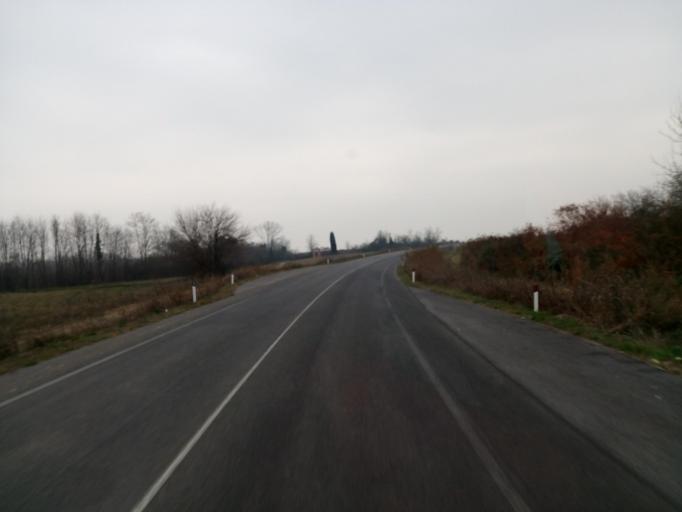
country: IT
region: Friuli Venezia Giulia
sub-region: Provincia di Udine
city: Pradamano
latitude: 46.0222
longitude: 13.3159
